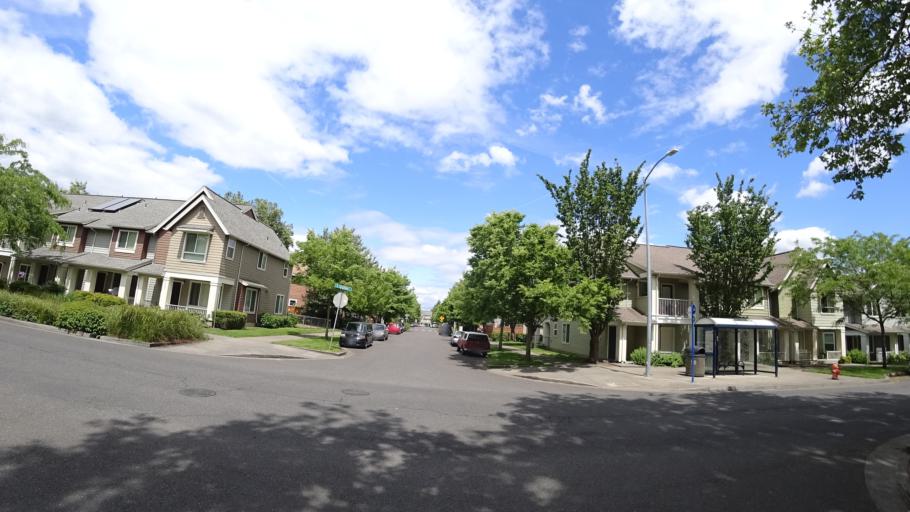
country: US
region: Washington
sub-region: Clark County
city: Vancouver
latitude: 45.5911
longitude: -122.7179
